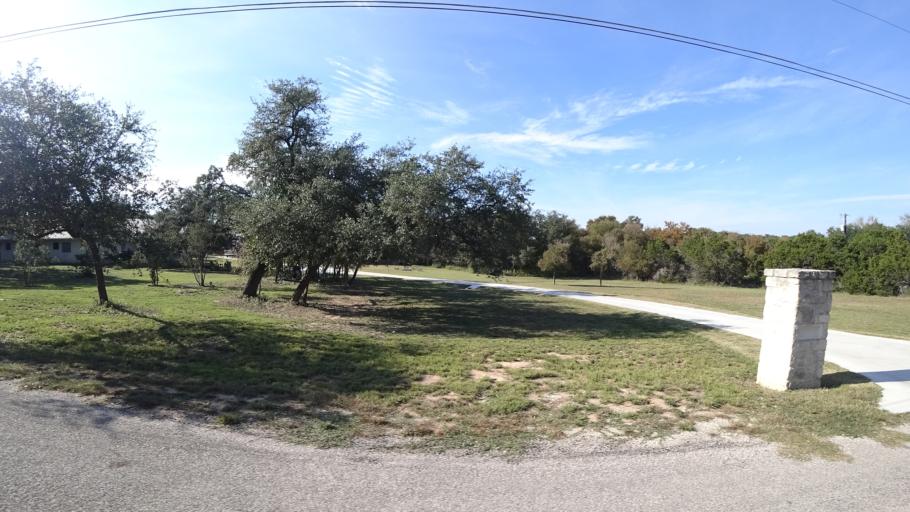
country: US
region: Texas
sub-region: Travis County
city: Bee Cave
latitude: 30.2354
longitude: -97.9414
